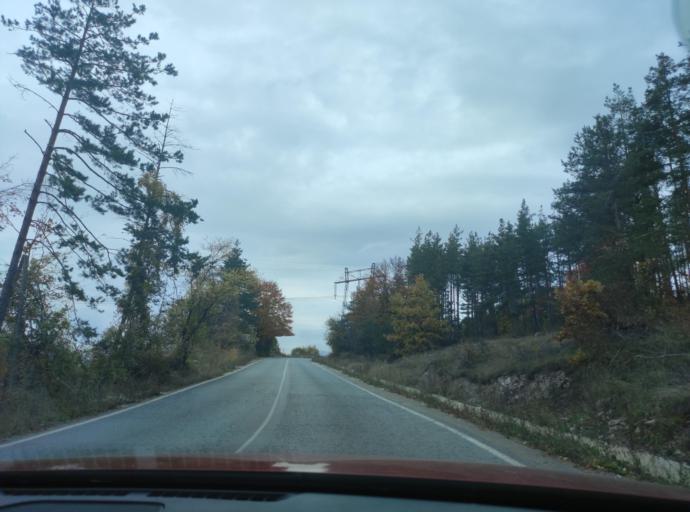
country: BG
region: Sofiya
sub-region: Obshtina Godech
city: Godech
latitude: 43.0192
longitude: 23.1308
